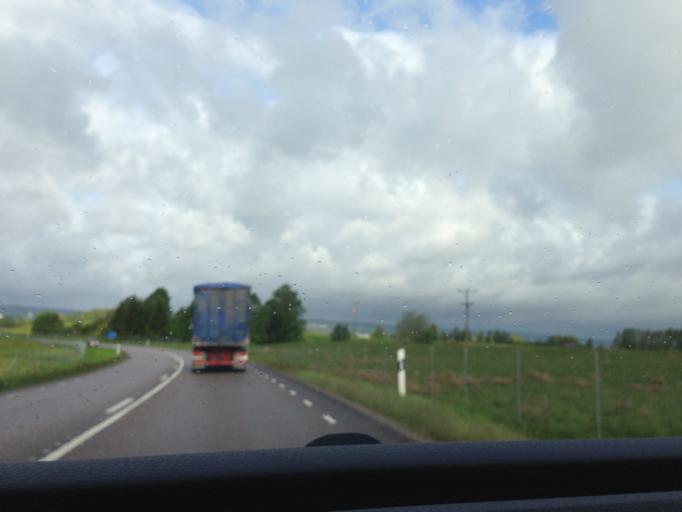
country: SE
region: Vaestra Goetaland
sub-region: Skovde Kommun
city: Skoevde
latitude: 58.3991
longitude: 13.9361
